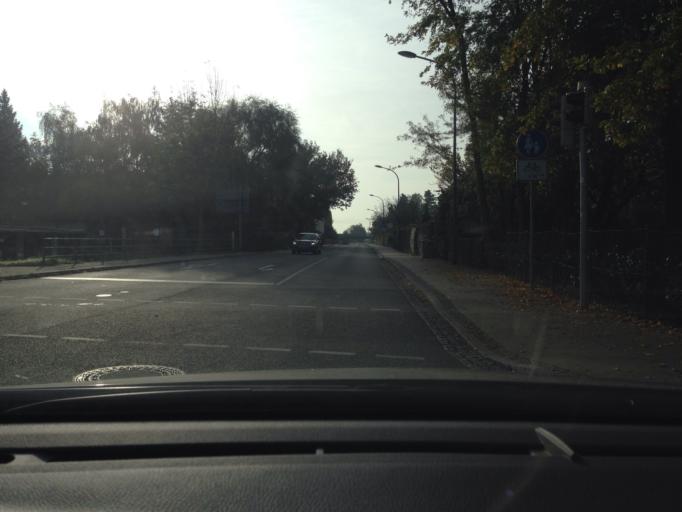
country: DE
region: Saxony
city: Borsdorf
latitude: 51.3491
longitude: 12.5460
